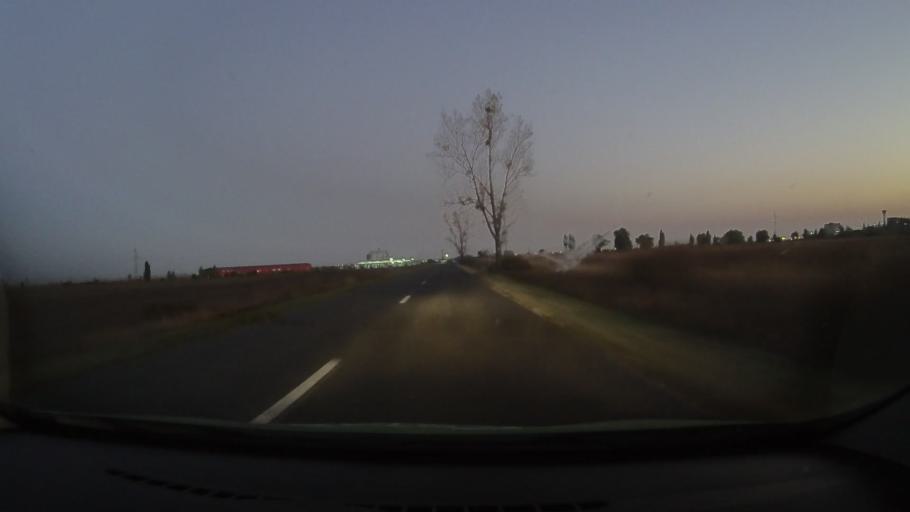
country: RO
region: Arad
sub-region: Comuna Vladimirescu
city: Vladimirescu
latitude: 46.1918
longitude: 21.3916
